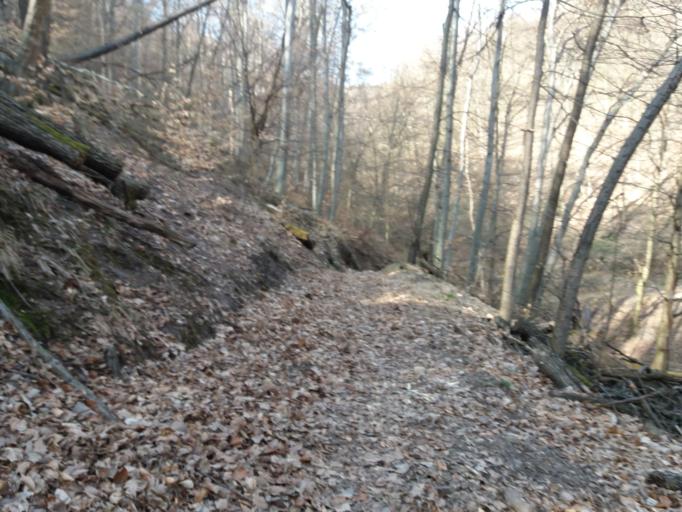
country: HU
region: Pest
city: Csobanka
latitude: 47.6784
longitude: 18.9726
